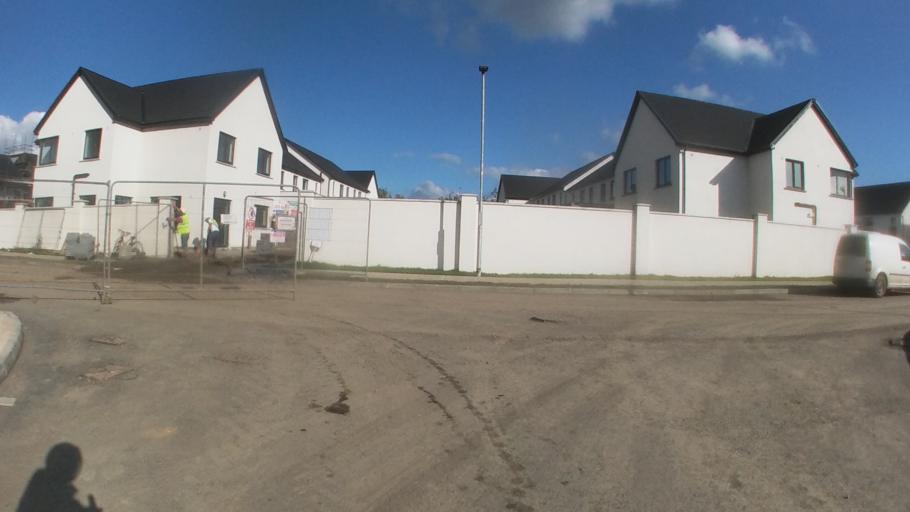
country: IE
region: Leinster
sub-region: Kilkenny
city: Kilkenny
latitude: 52.6722
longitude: -7.2342
